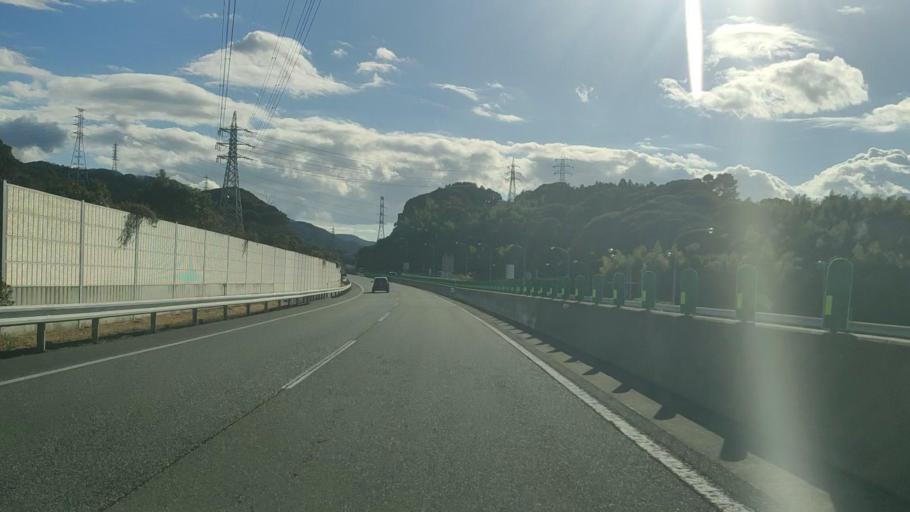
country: JP
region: Fukuoka
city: Kitakyushu
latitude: 33.8418
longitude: 130.7655
